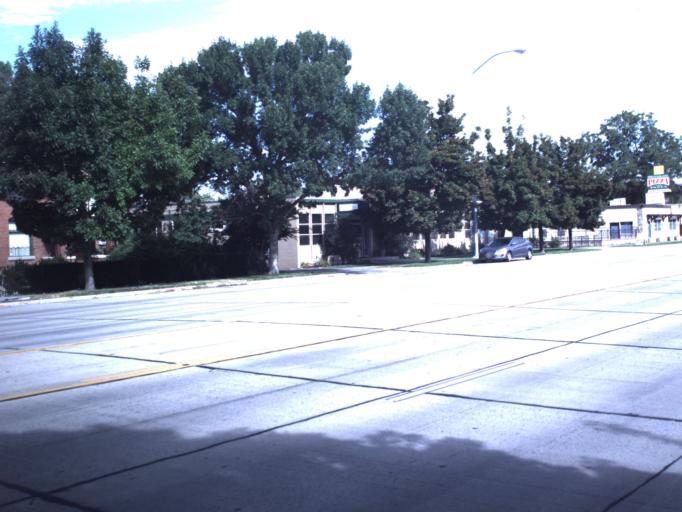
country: US
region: Utah
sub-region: Weber County
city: Ogden
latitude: 41.2416
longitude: -111.9699
